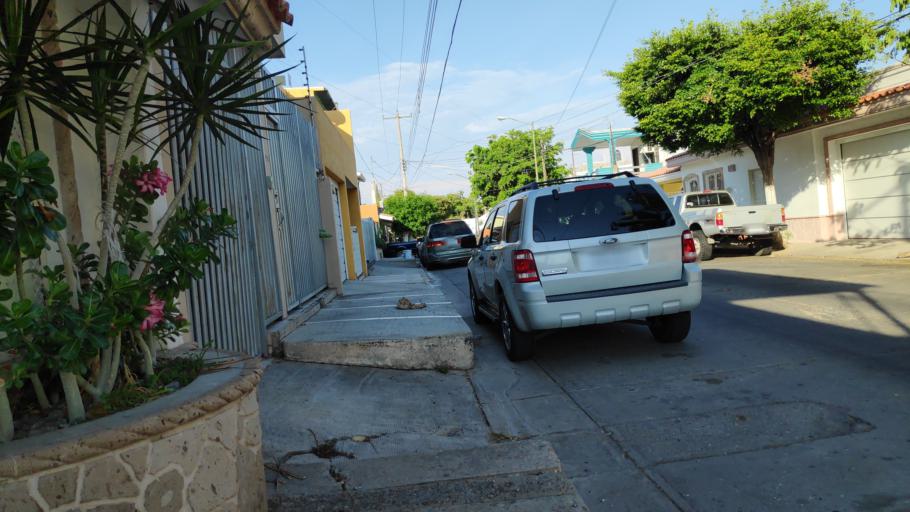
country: MX
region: Sinaloa
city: Culiacan
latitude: 24.7904
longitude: -107.4036
